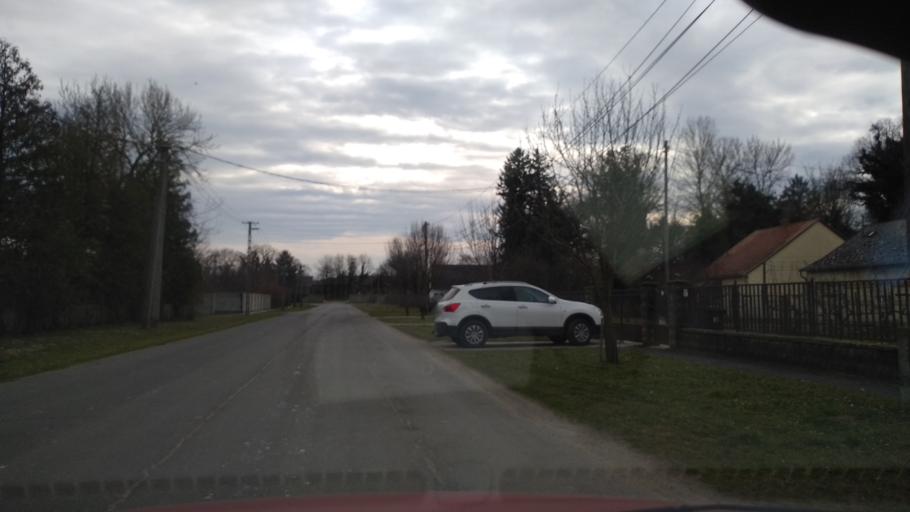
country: HU
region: Somogy
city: Barcs
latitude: 45.9548
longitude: 17.4412
